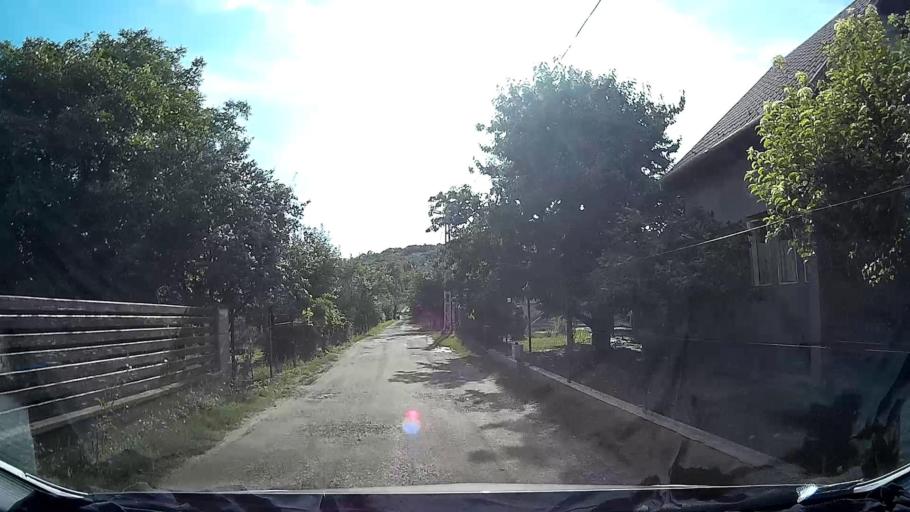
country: HU
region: Pest
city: Nagykovacsi
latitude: 47.6612
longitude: 19.0198
